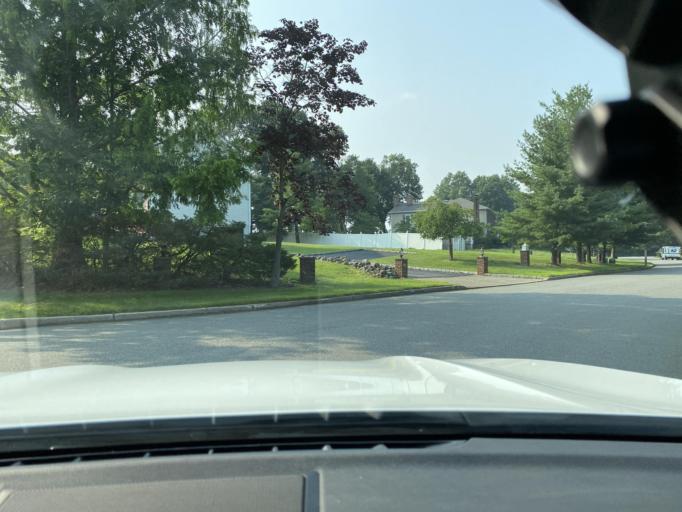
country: US
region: New York
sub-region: Rockland County
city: Airmont
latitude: 41.0885
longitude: -74.1230
